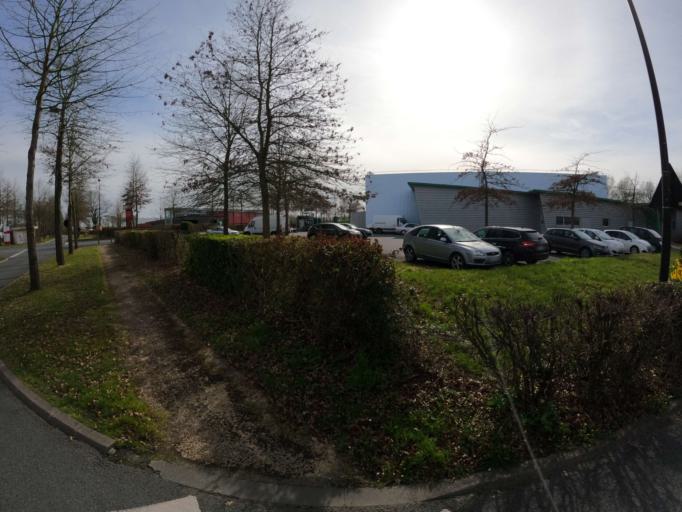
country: FR
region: Pays de la Loire
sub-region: Departement de la Vendee
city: Bouffere
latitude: 46.9552
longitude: -1.3523
